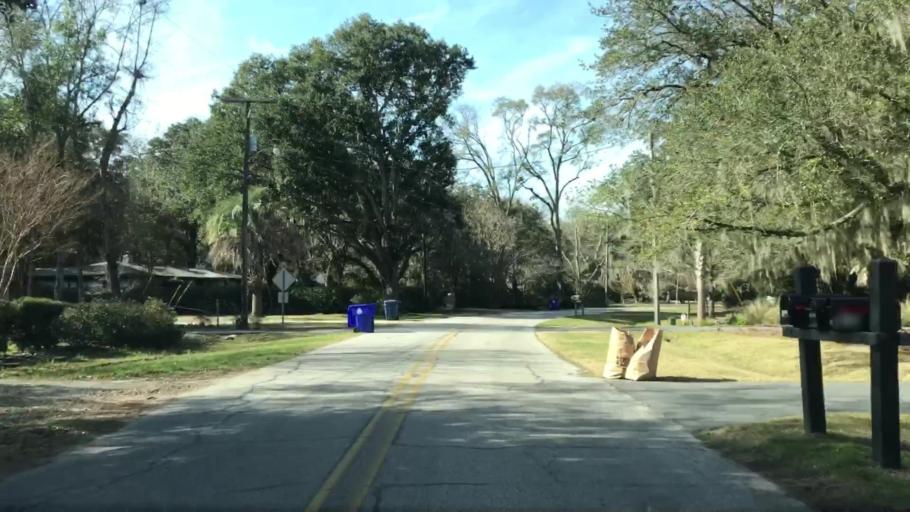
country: US
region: South Carolina
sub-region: Charleston County
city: Charleston
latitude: 32.7703
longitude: -79.9978
